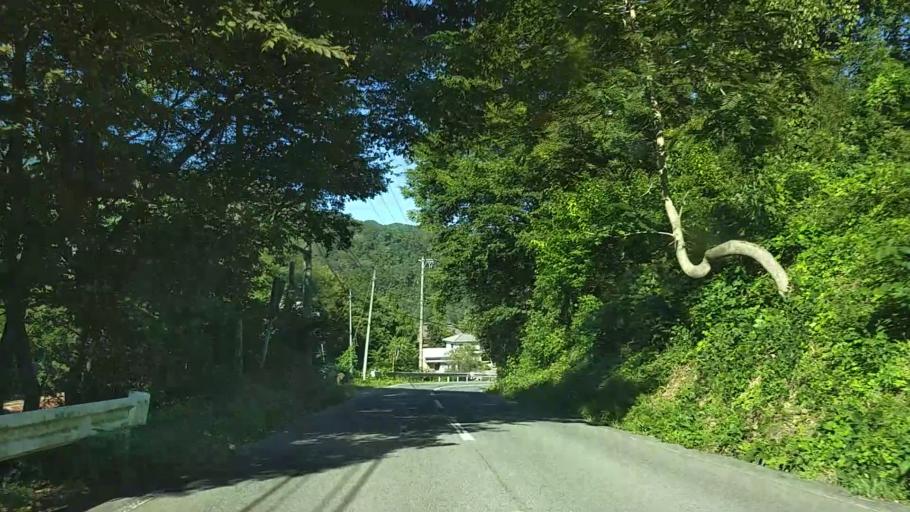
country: JP
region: Nagano
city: Nagano-shi
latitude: 36.6146
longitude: 138.0913
